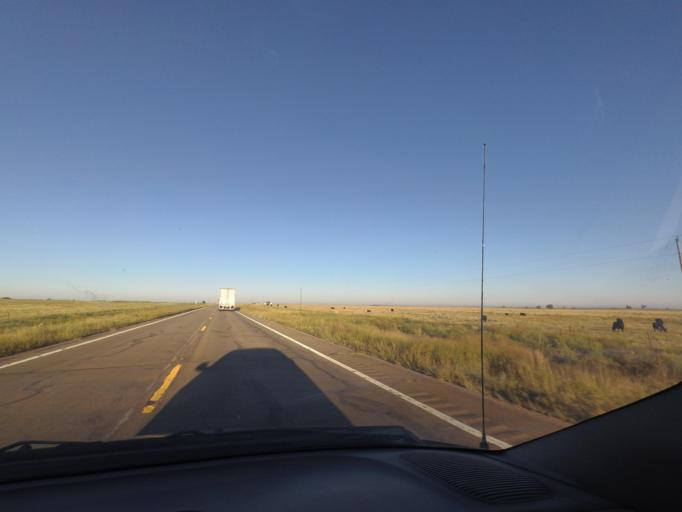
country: US
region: Colorado
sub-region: Yuma County
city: Yuma
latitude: 39.6701
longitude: -102.8896
